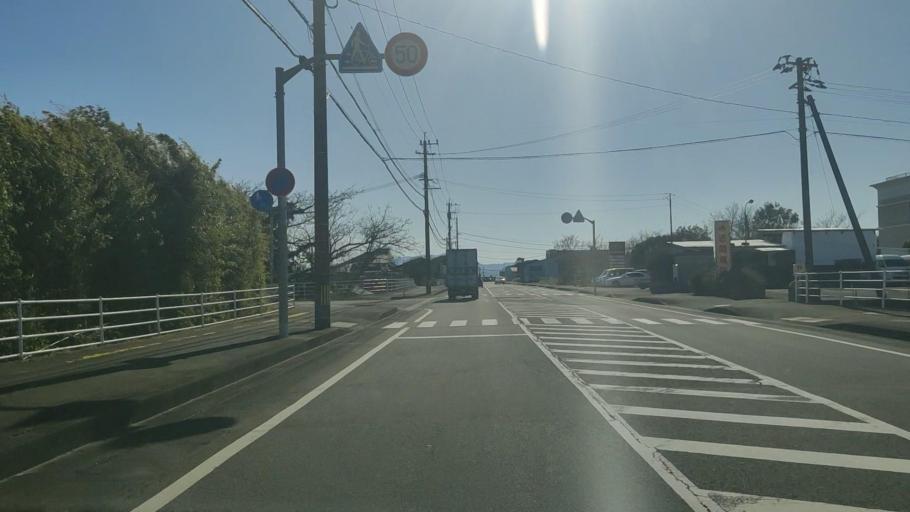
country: JP
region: Miyazaki
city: Miyazaki-shi
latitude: 31.9475
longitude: 131.4595
